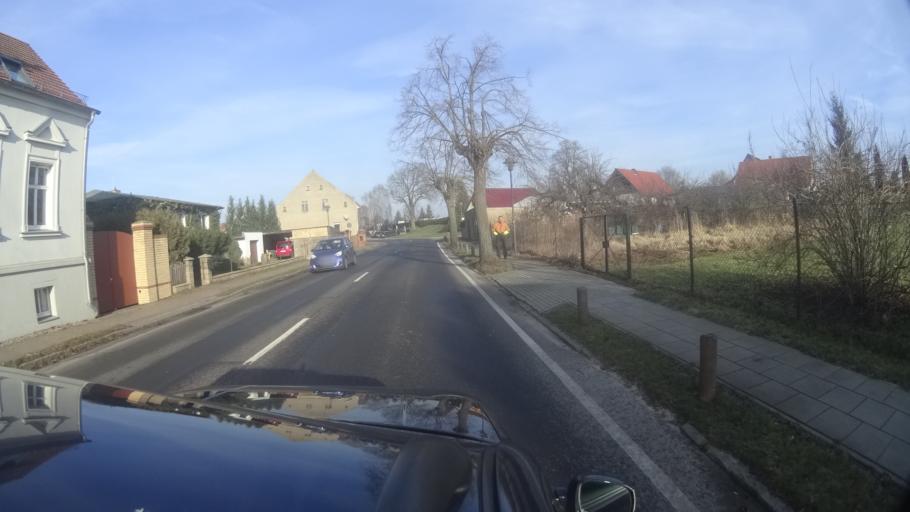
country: DE
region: Brandenburg
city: Kremmen
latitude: 52.7237
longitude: 13.0971
